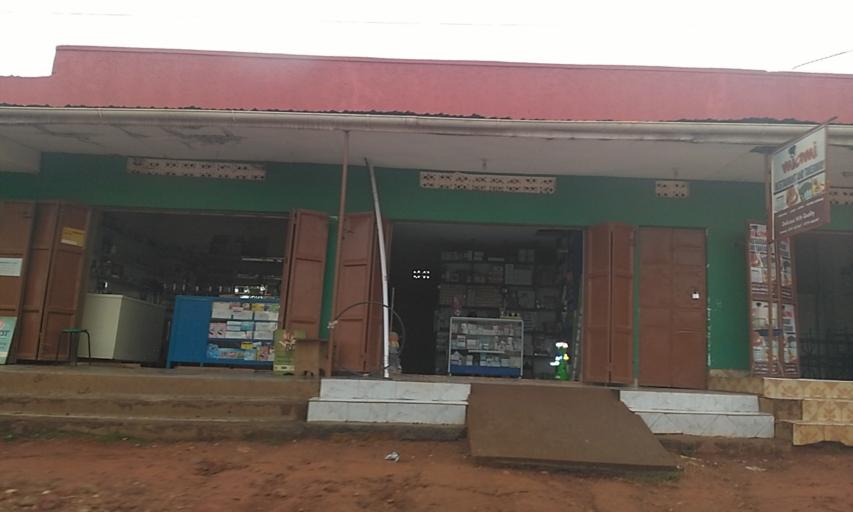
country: UG
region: Central Region
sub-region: Wakiso District
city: Bweyogerere
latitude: 0.3562
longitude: 32.6653
